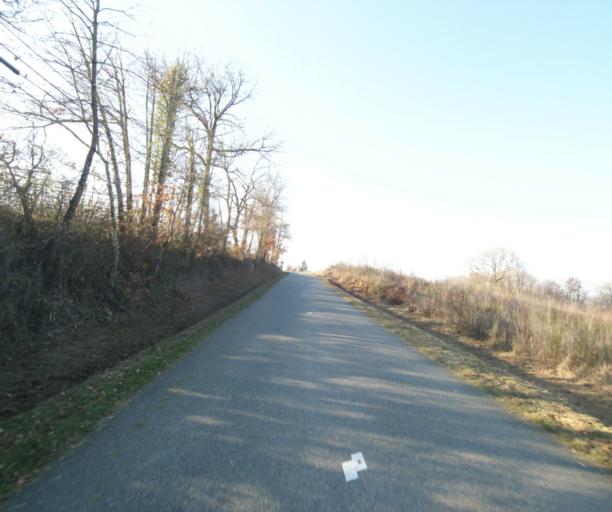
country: FR
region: Midi-Pyrenees
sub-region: Departement du Tarn-et-Garonne
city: Moissac
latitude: 44.1447
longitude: 1.0551
